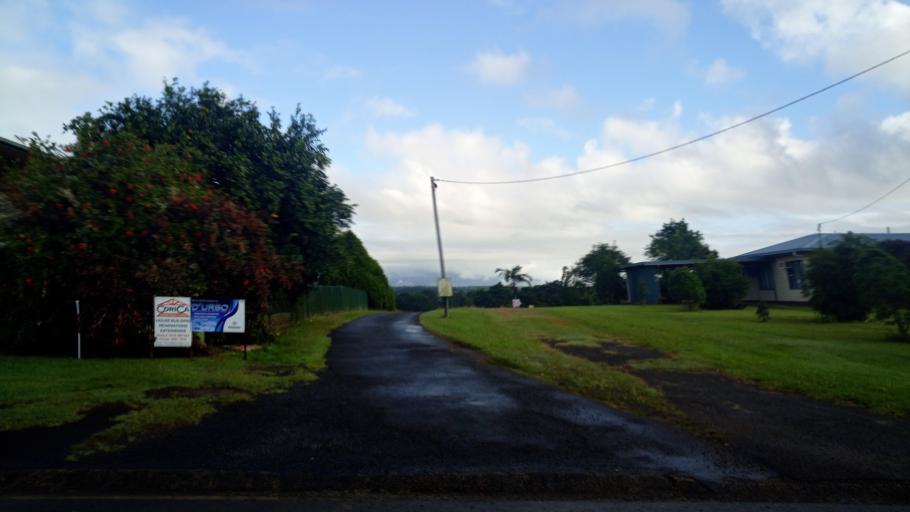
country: AU
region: Queensland
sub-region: Cassowary Coast
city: Innisfail
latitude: -17.5163
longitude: 145.9896
